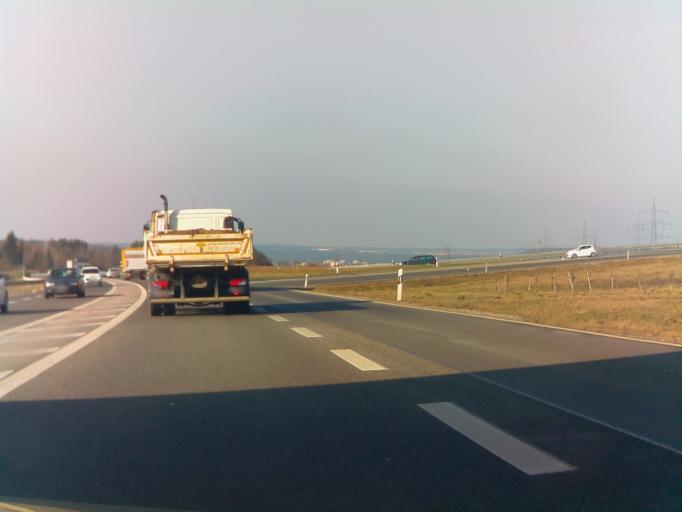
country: DE
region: Baden-Wuerttemberg
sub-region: Regierungsbezirk Stuttgart
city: Magstadt
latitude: 48.7361
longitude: 8.9506
